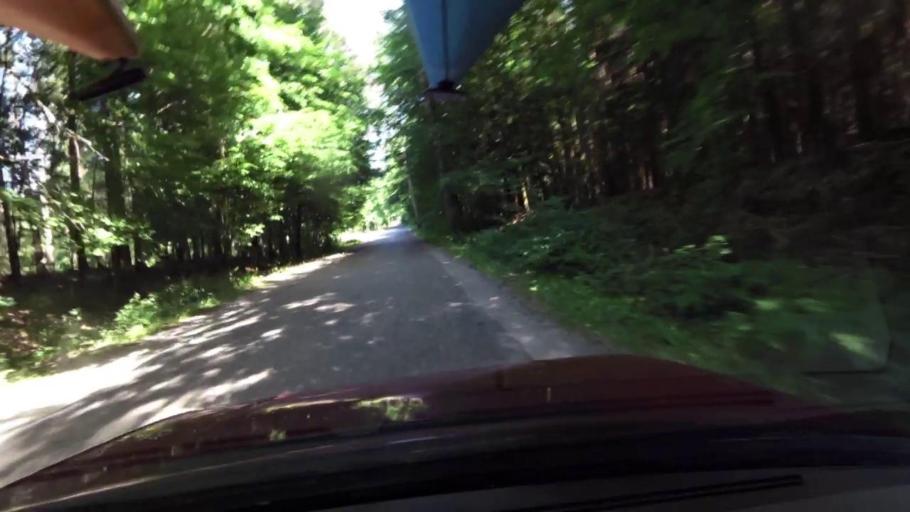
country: PL
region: Pomeranian Voivodeship
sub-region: Powiat slupski
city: Kepice
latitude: 54.1659
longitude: 16.8997
